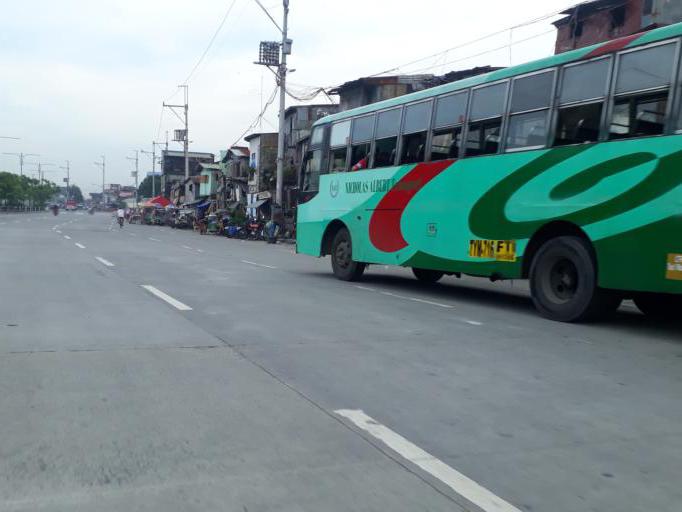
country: PH
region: Metro Manila
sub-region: Caloocan City
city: Niugan
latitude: 14.6463
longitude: 120.9511
